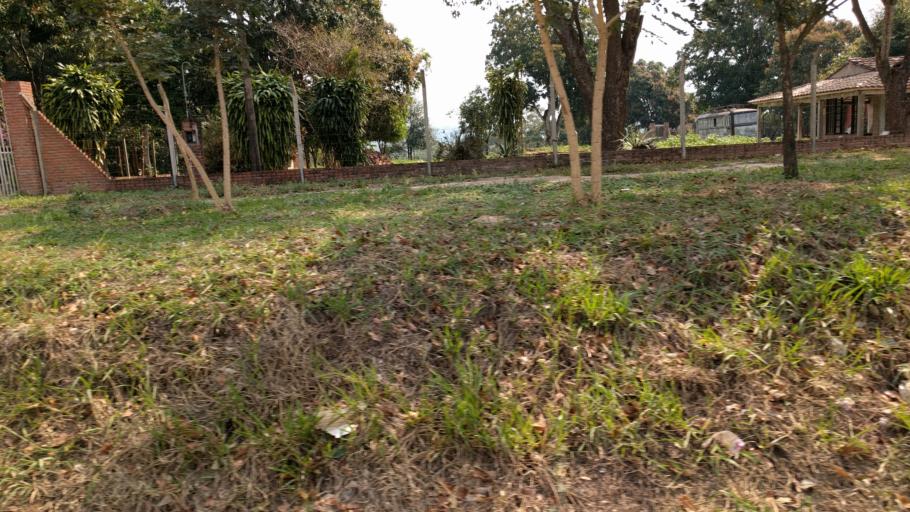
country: BO
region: Santa Cruz
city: Santa Rita
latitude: -17.9090
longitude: -63.3415
